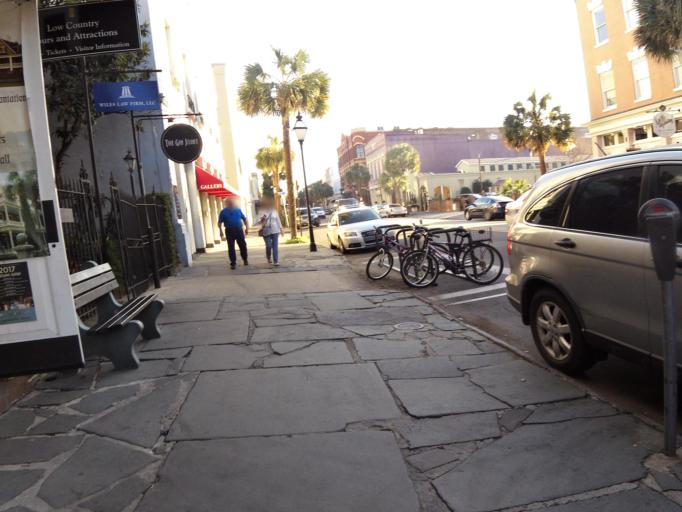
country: US
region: South Carolina
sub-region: Charleston County
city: Charleston
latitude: 32.7795
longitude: -79.9271
